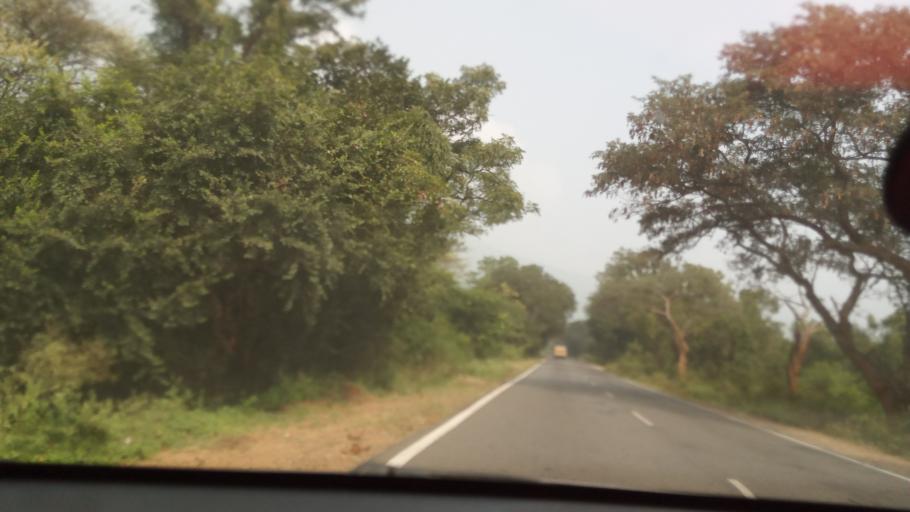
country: IN
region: Tamil Nadu
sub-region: Erode
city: Sathyamangalam
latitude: 11.5785
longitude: 77.1329
